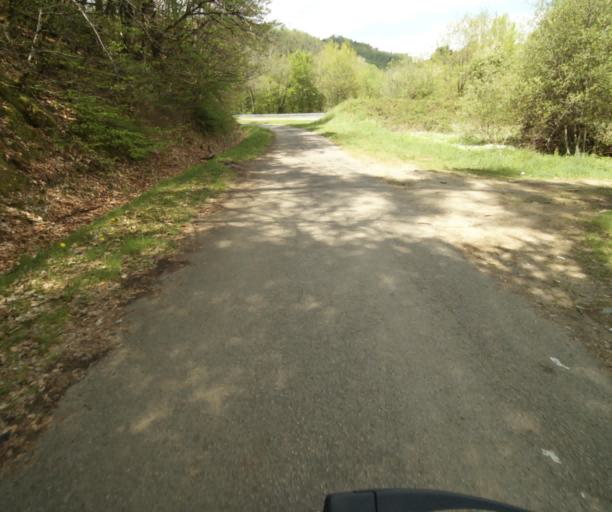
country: FR
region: Limousin
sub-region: Departement de la Correze
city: Naves
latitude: 45.2937
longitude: 1.7760
